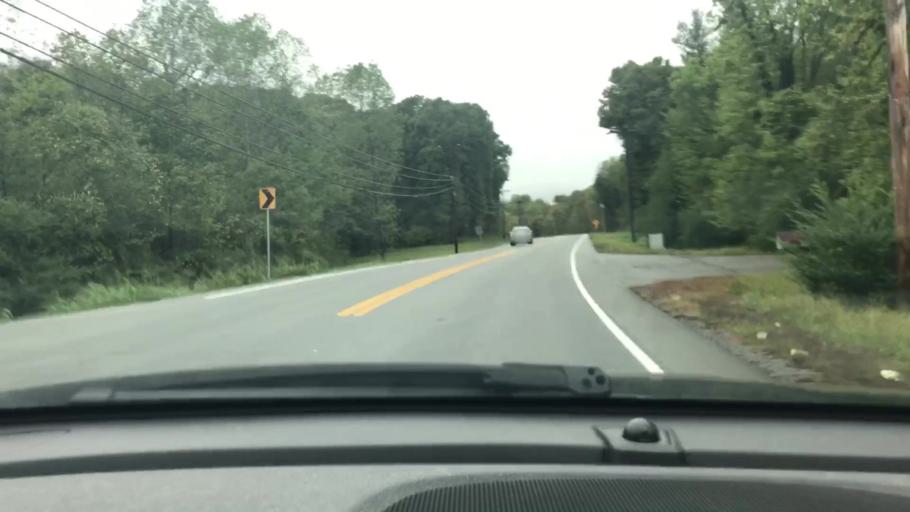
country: US
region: Tennessee
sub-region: Dickson County
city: White Bluff
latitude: 36.1086
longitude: -87.1685
